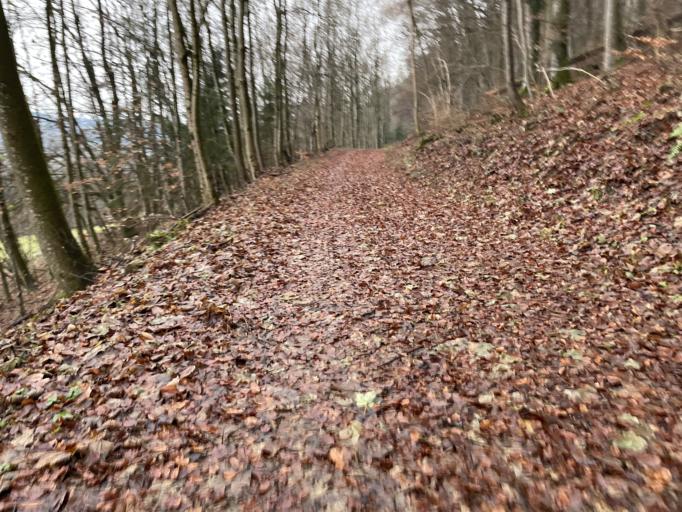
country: CH
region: Bern
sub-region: Bern-Mittelland District
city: Munsingen
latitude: 46.8726
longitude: 7.5355
